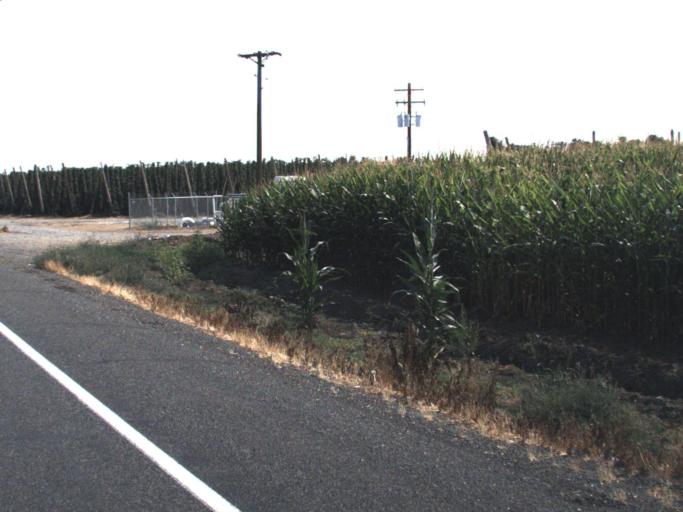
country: US
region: Washington
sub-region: Yakima County
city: Granger
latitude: 46.2894
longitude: -120.1786
